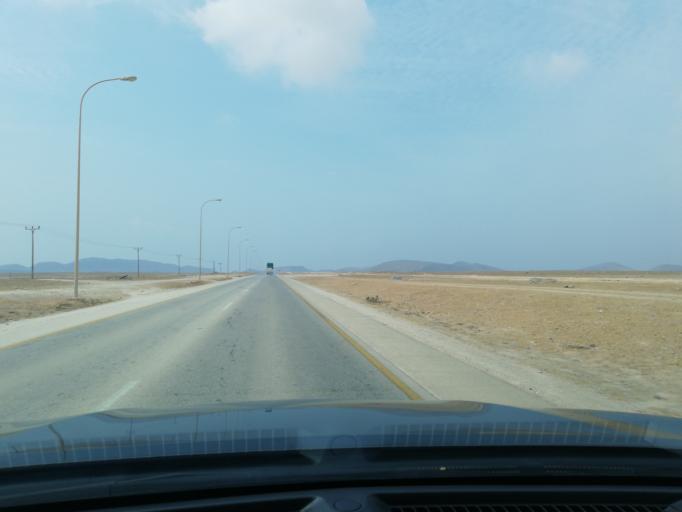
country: OM
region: Zufar
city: Salalah
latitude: 16.9324
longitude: 53.8432
